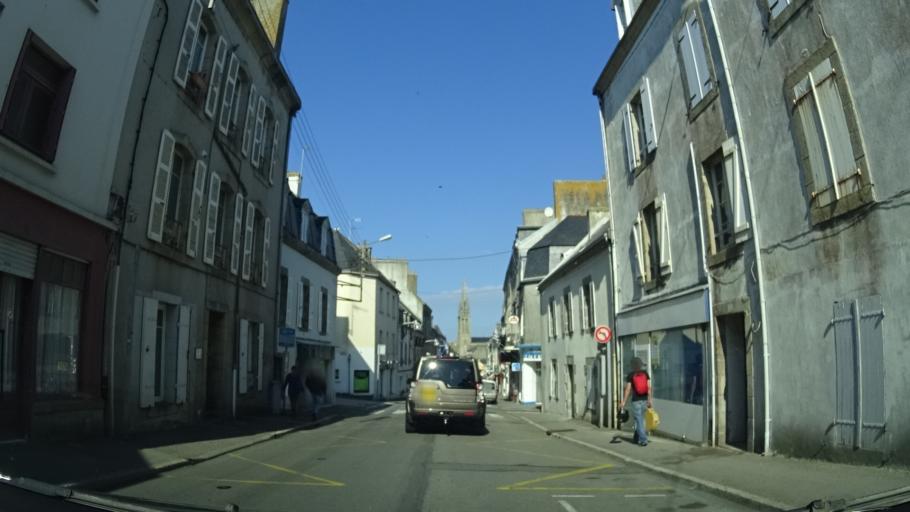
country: FR
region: Brittany
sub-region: Departement du Finistere
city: Douarnenez
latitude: 48.0921
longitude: -4.3280
